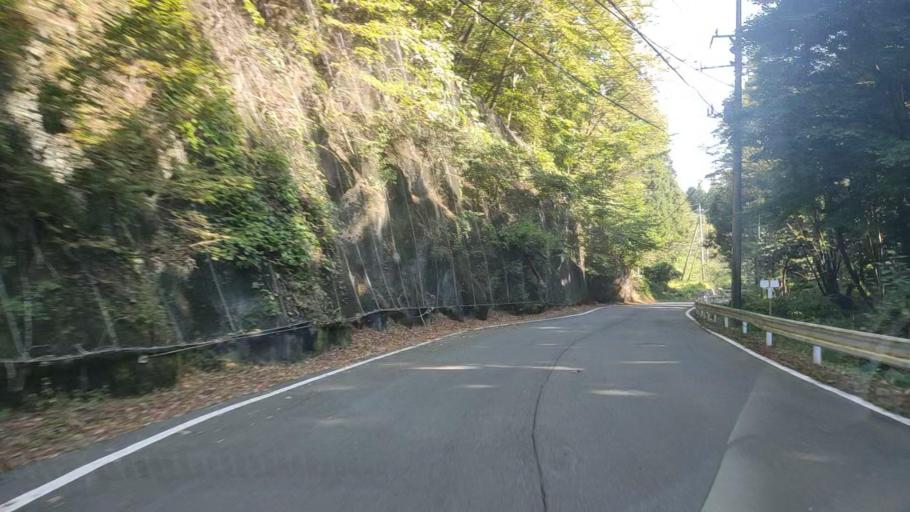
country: JP
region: Gunma
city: Nakanojomachi
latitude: 36.6005
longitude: 138.7116
